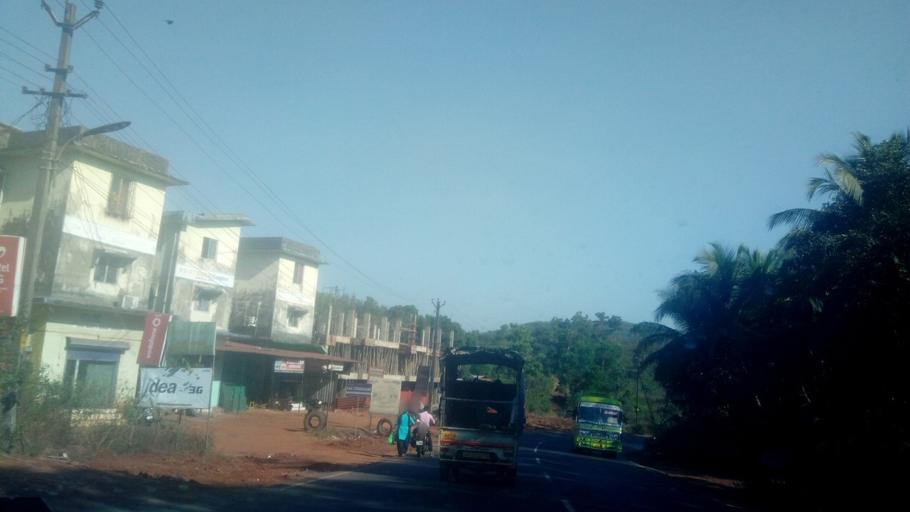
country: IN
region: Goa
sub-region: North Goa
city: Jua
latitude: 15.5083
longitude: 73.9622
